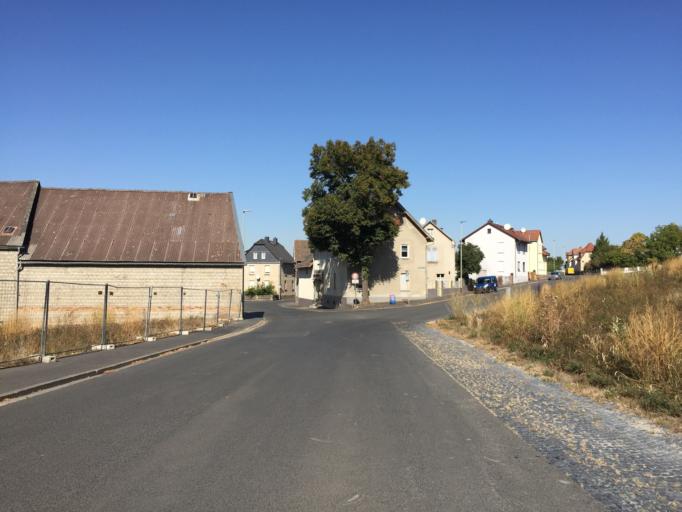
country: DE
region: Hesse
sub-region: Regierungsbezirk Giessen
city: Hungen
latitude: 50.4280
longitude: 8.9367
